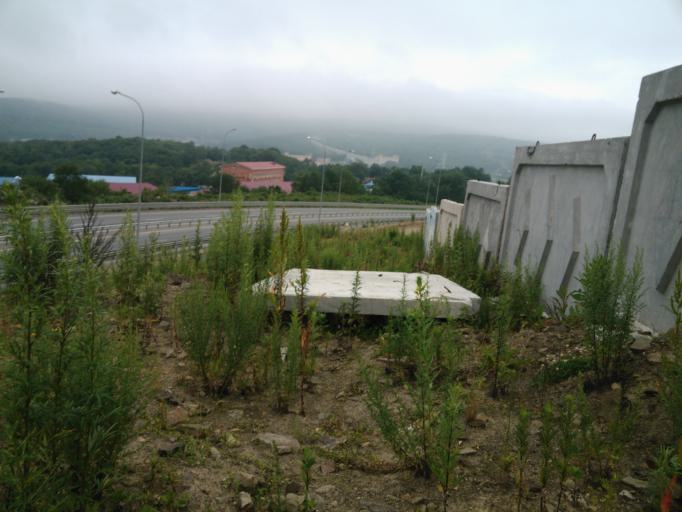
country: RU
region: Primorskiy
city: Vladivostok
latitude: 43.0975
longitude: 131.9830
